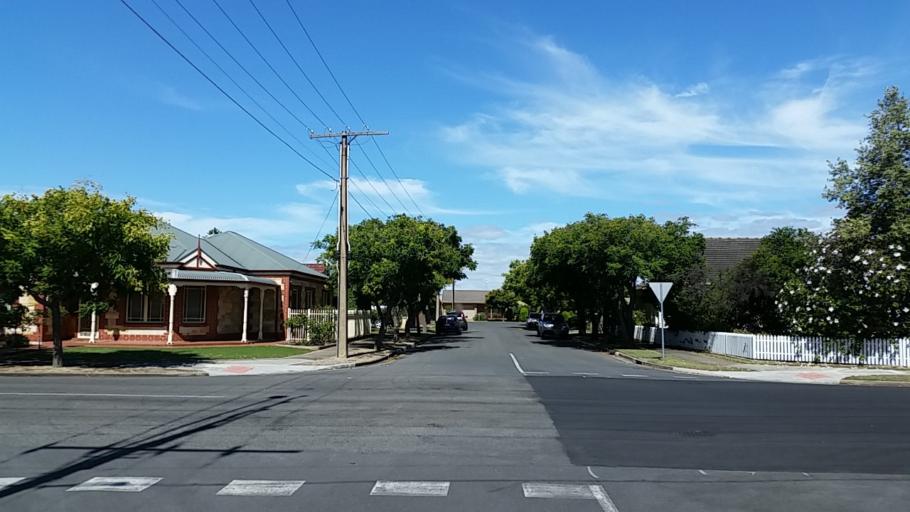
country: AU
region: South Australia
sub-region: Charles Sturt
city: Seaton
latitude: -34.9225
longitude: 138.5231
